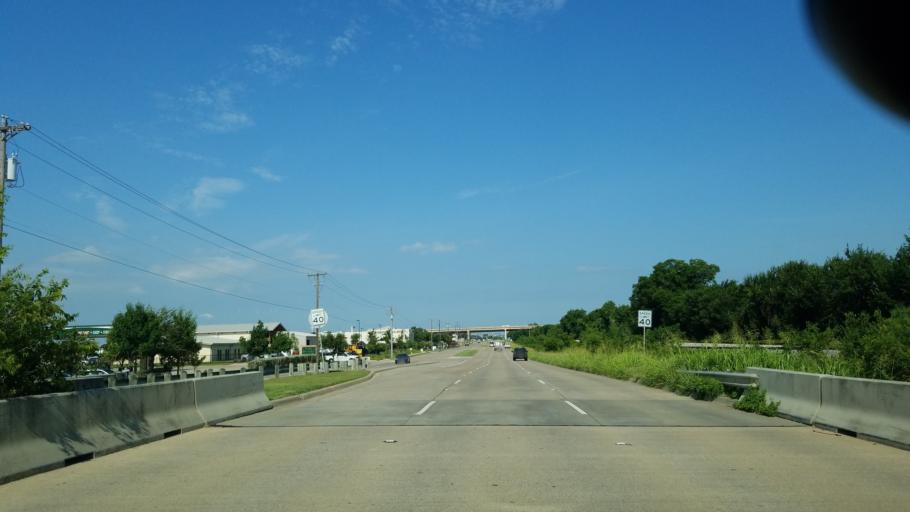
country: US
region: Texas
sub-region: Dallas County
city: Carrollton
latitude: 32.9523
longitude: -96.9175
